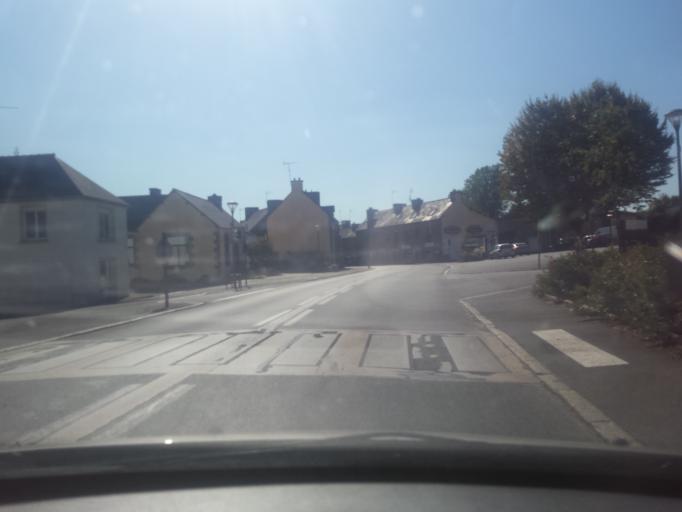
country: FR
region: Brittany
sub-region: Departement des Cotes-d'Armor
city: Plounevez-Quintin
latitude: 48.2907
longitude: -3.2309
